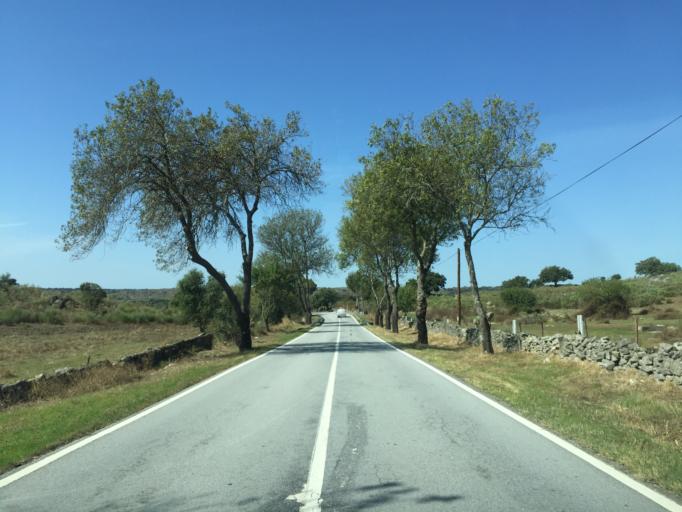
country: PT
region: Portalegre
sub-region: Castelo de Vide
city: Castelo de Vide
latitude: 39.4358
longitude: -7.5154
